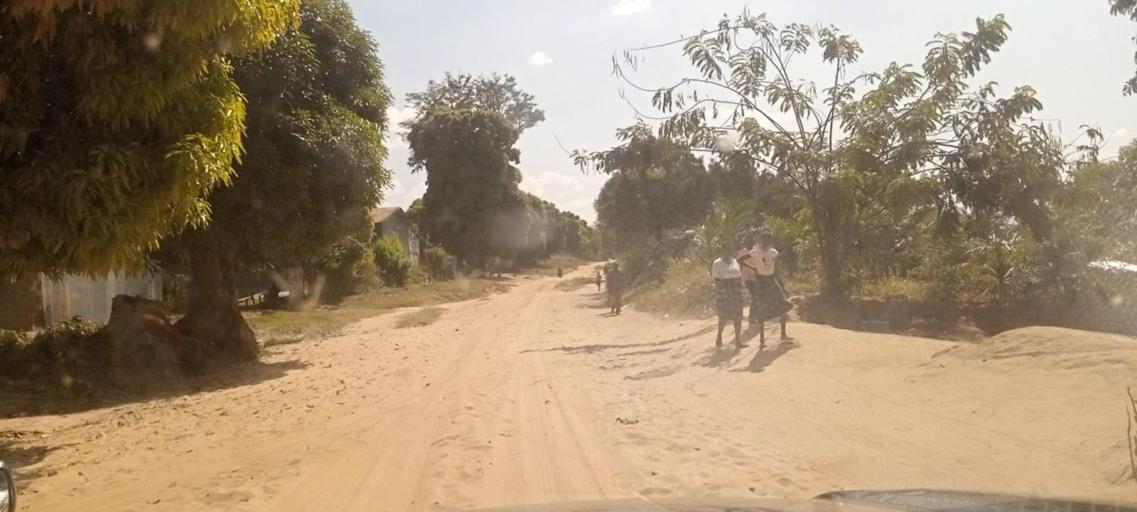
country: CD
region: Kasai-Oriental
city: Kabinda
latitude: -6.1333
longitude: 24.5115
